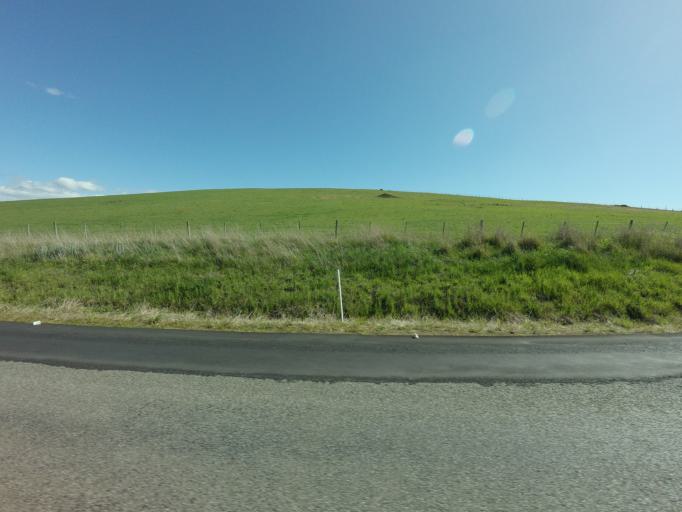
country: AU
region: Tasmania
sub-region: Derwent Valley
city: New Norfolk
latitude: -42.6467
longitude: 146.9245
